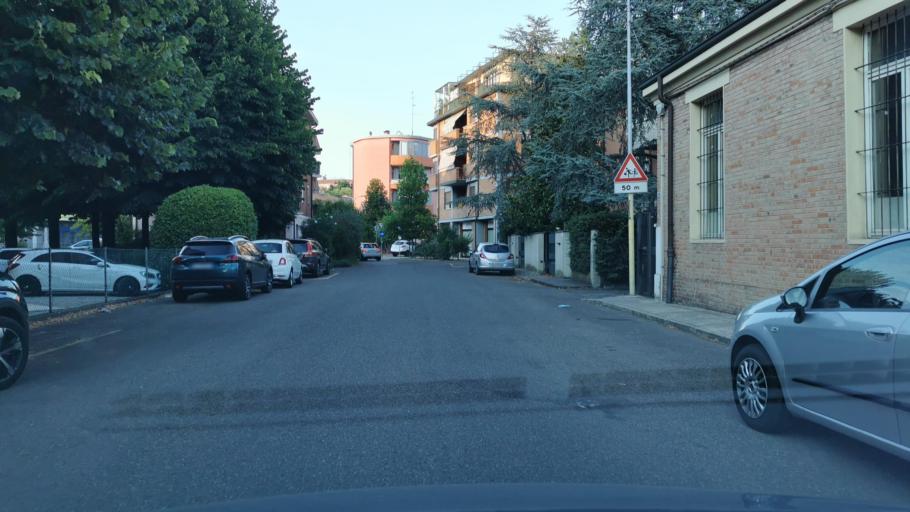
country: IT
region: Emilia-Romagna
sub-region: Provincia di Modena
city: Modena
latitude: 44.6340
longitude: 10.9277
